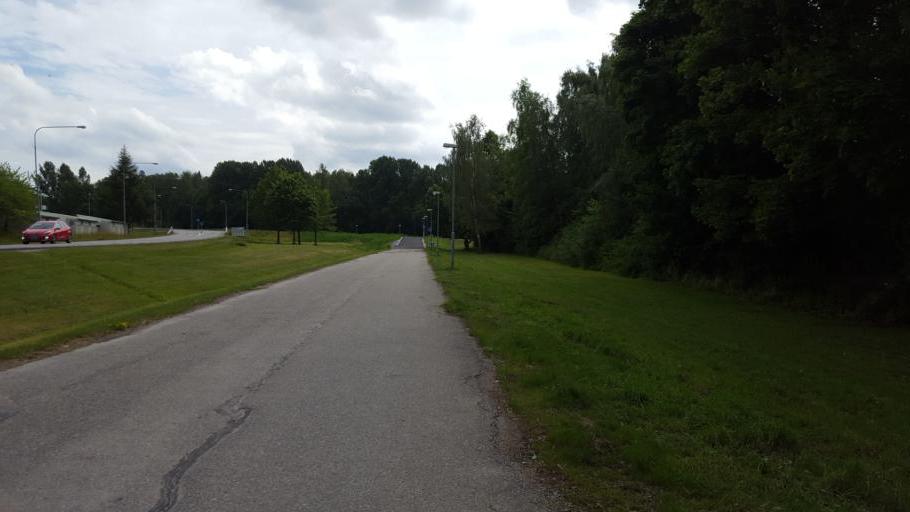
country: SE
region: Stockholm
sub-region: Upplands Vasby Kommun
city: Upplands Vaesby
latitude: 59.5083
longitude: 17.9006
